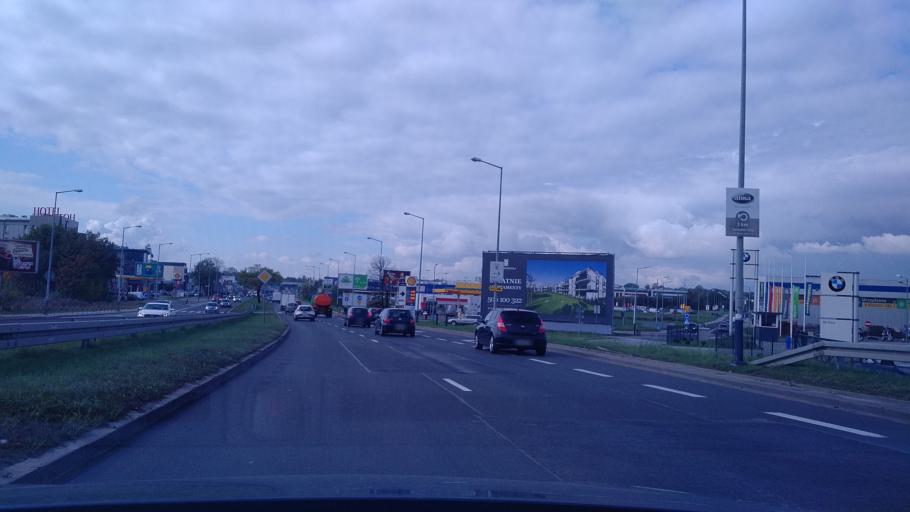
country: PL
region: Lesser Poland Voivodeship
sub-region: Powiat krakowski
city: Zielonki
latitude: 50.0895
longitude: 19.9049
